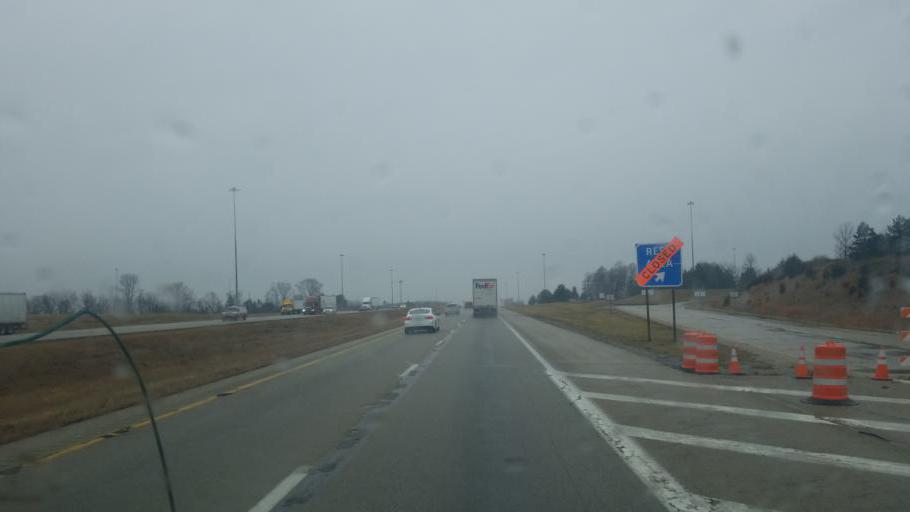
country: US
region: Ohio
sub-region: Preble County
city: New Paris
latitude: 39.8288
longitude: -84.7545
